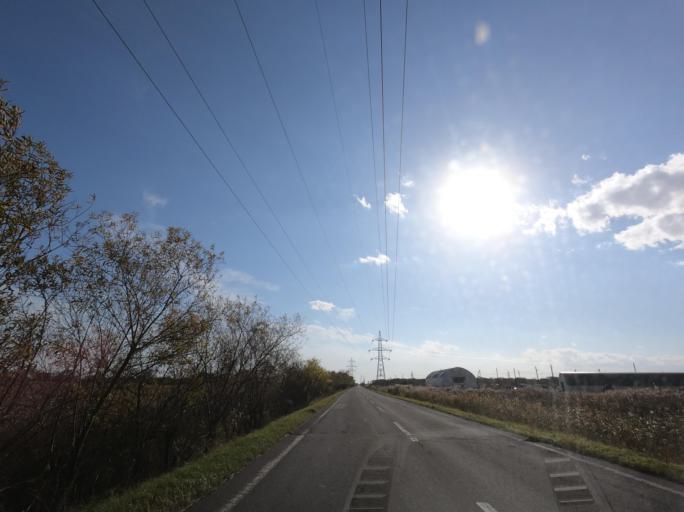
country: JP
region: Hokkaido
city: Kushiro
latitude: 43.0508
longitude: 144.3229
